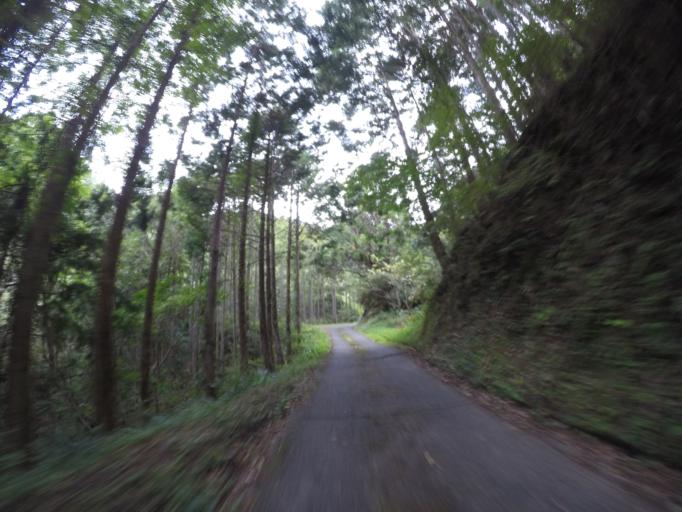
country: JP
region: Shizuoka
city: Shimada
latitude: 34.8893
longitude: 138.1646
